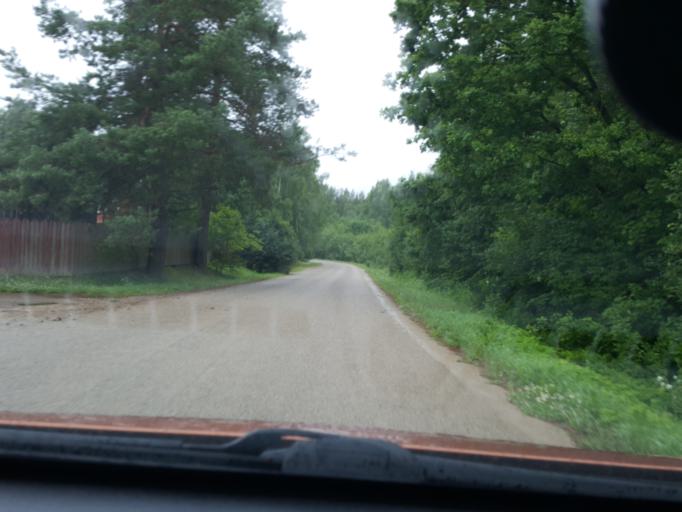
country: LV
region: Ikskile
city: Ikskile
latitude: 56.8931
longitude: 24.5030
